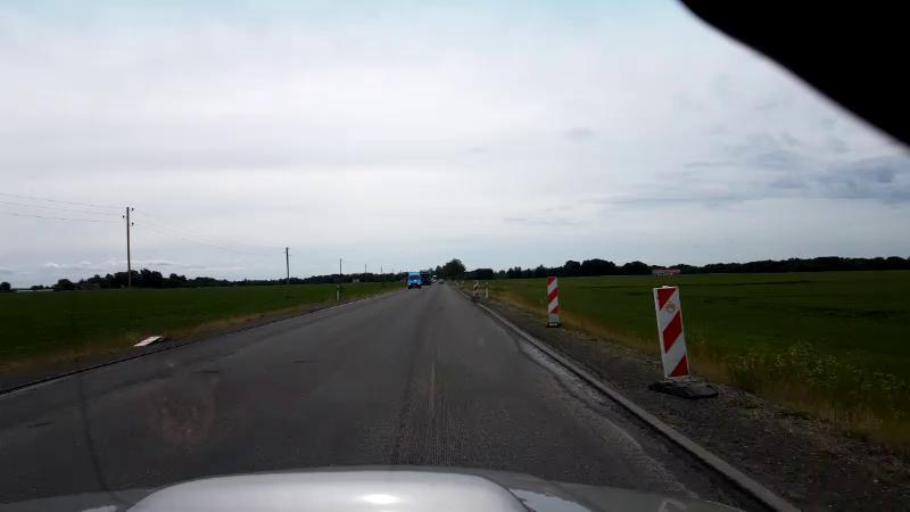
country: LV
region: Bauskas Rajons
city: Bauska
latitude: 56.3364
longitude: 24.2959
